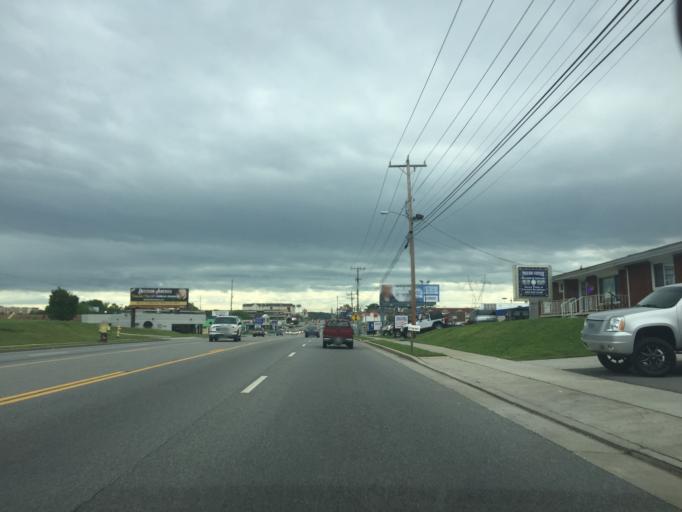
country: US
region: Tennessee
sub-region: Hamilton County
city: East Brainerd
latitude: 35.0460
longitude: -85.1658
